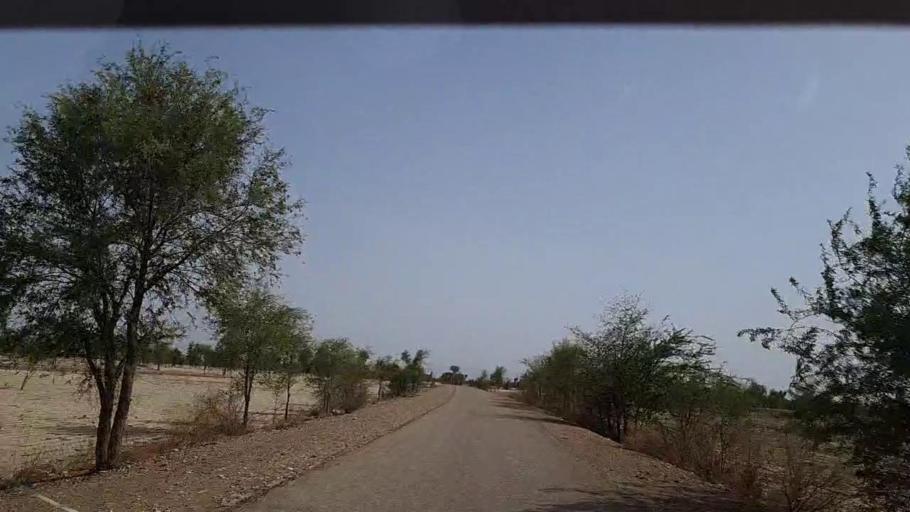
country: PK
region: Sindh
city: Johi
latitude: 26.6329
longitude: 67.5016
